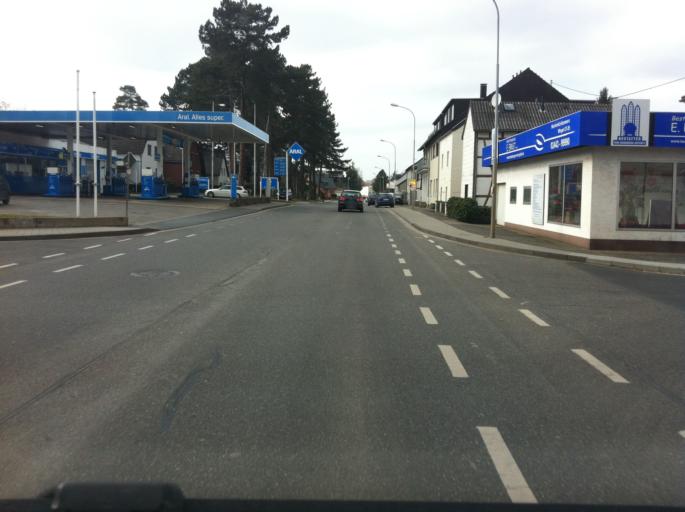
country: DE
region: North Rhine-Westphalia
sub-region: Regierungsbezirk Koln
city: Mechernich
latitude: 50.5883
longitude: 6.6481
